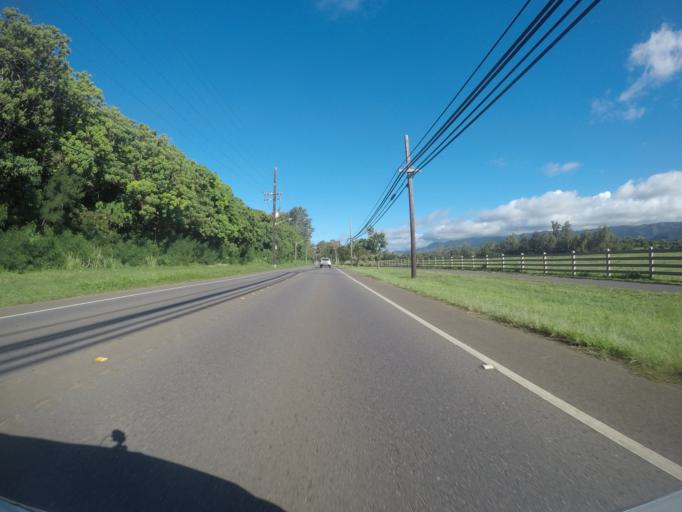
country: US
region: Hawaii
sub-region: Honolulu County
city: La'ie
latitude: 21.6592
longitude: -157.9326
